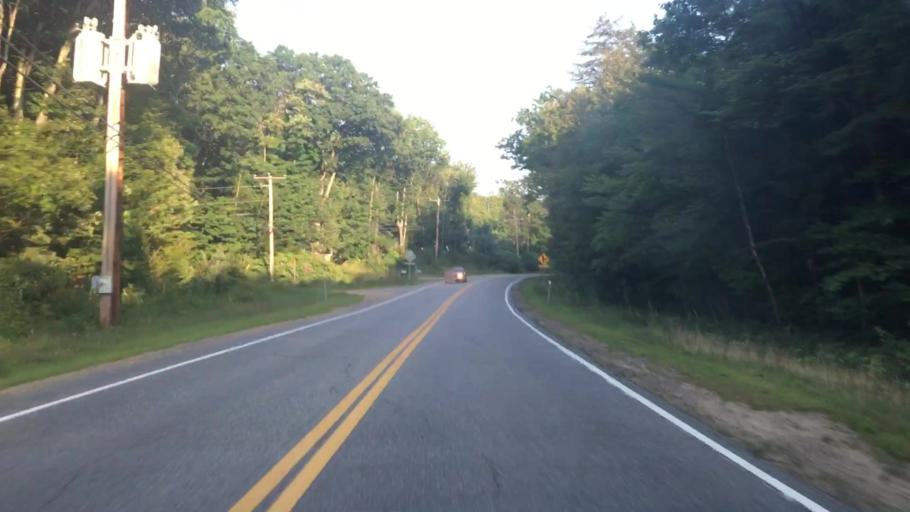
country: US
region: New Hampshire
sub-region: Belknap County
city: Laconia
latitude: 43.4954
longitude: -71.4430
